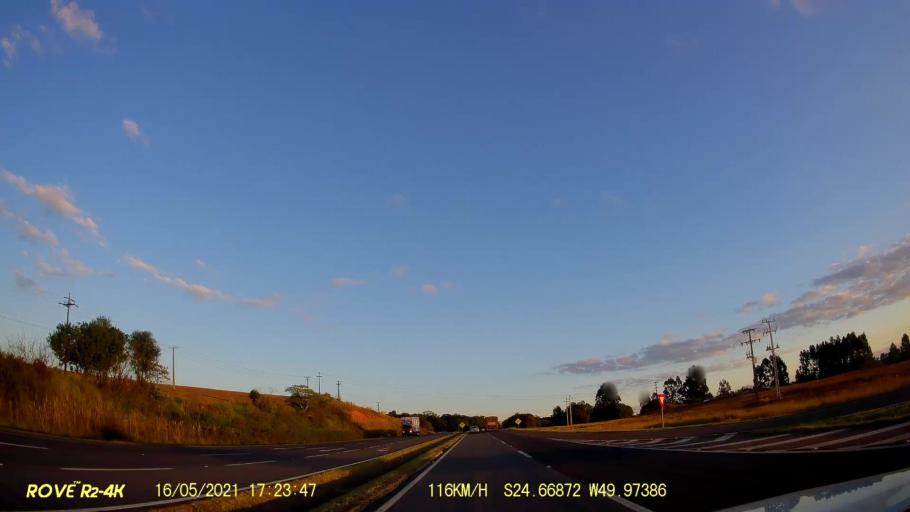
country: BR
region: Parana
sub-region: Castro
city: Castro
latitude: -24.6690
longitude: -49.9738
